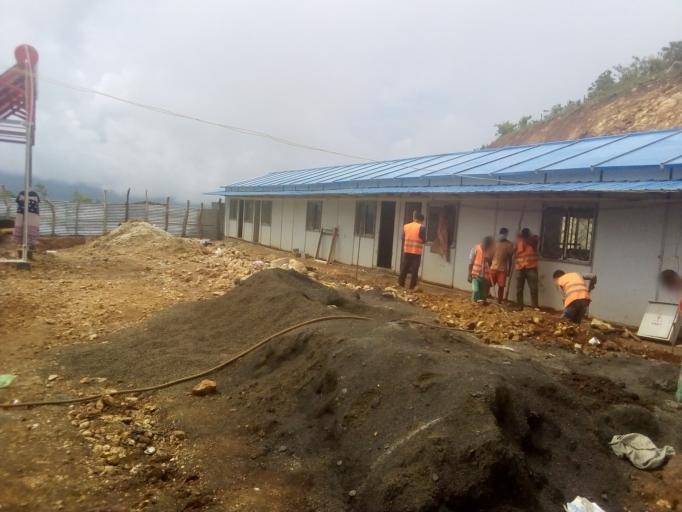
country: ET
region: Southern Nations, Nationalities, and People's Region
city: Areka
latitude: 7.2269
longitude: 37.2629
